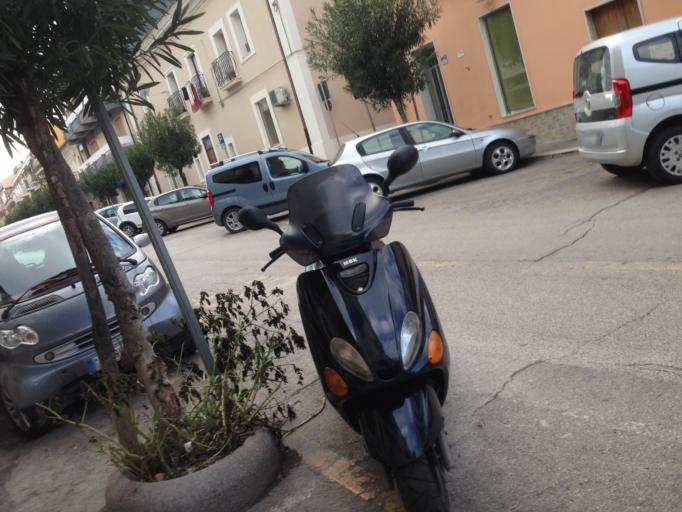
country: IT
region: Molise
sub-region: Provincia di Campobasso
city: Termoli
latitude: 42.0028
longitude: 14.9968
